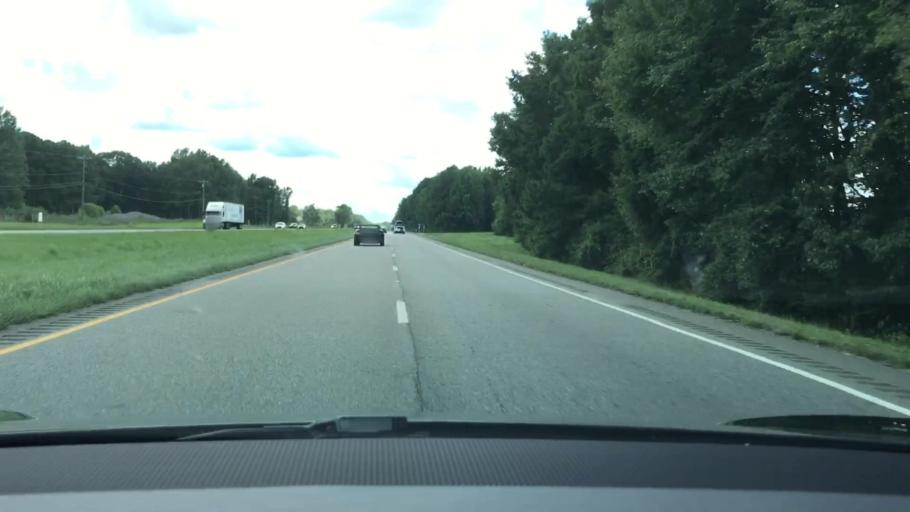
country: US
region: Alabama
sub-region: Montgomery County
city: Pike Road
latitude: 32.1812
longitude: -86.1174
